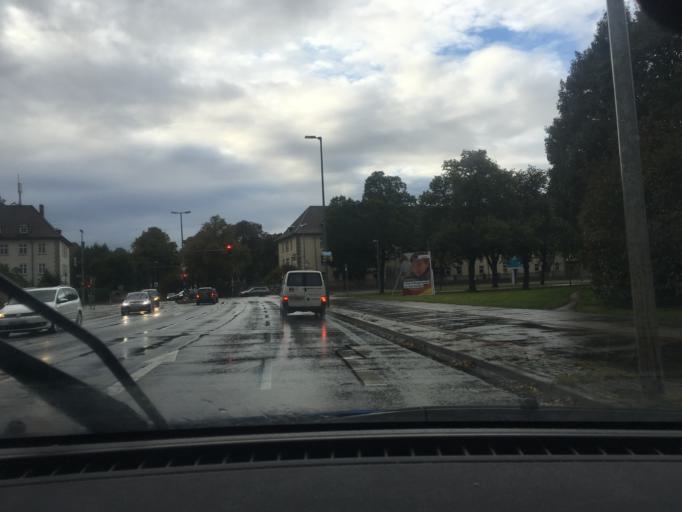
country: DE
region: Lower Saxony
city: Langenhagen
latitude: 52.4152
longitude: 9.7946
